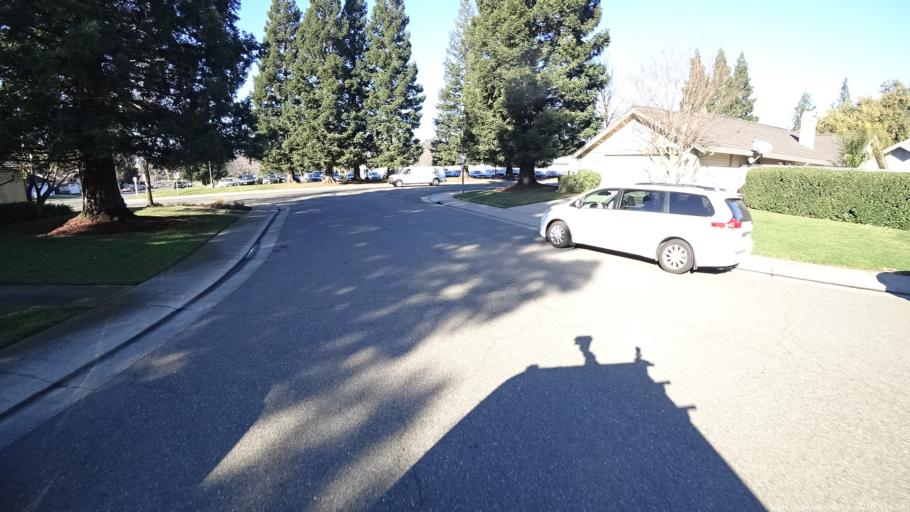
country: US
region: California
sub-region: Sacramento County
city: Gold River
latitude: 38.6264
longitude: -121.2476
